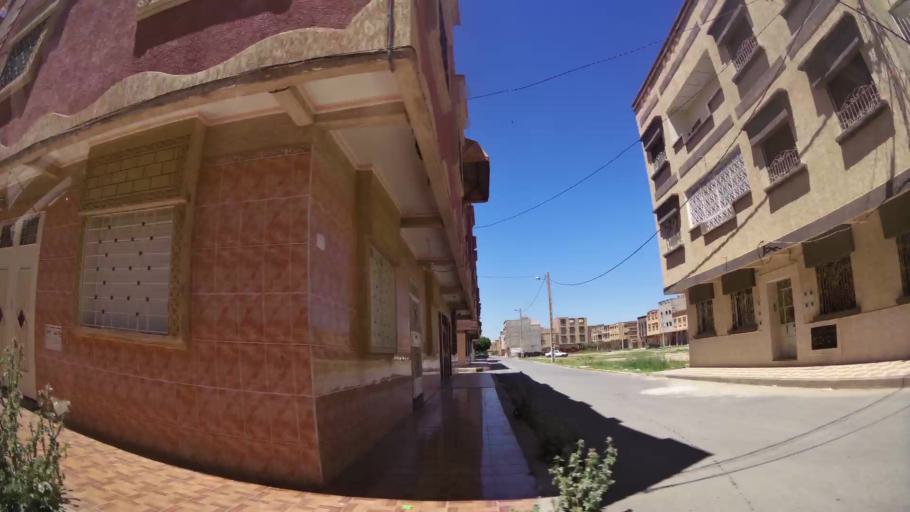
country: MA
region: Oriental
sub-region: Oujda-Angad
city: Oujda
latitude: 34.6735
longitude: -1.8828
